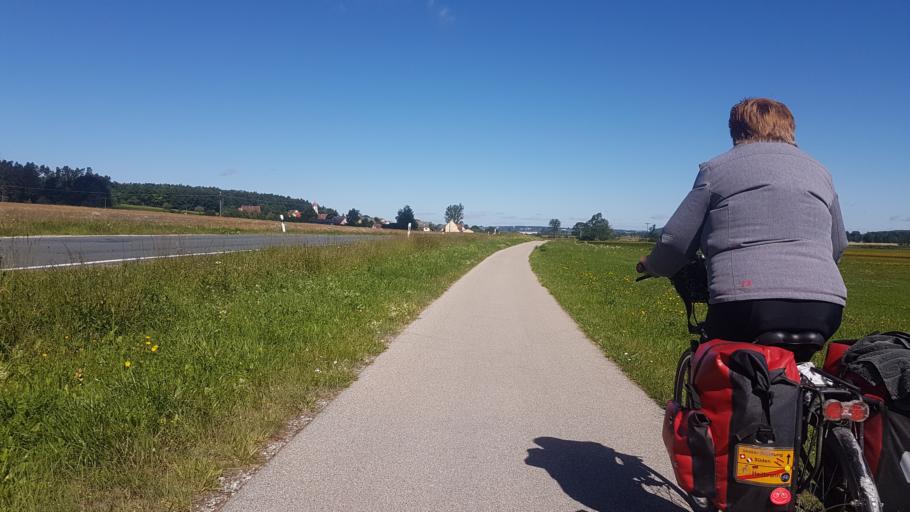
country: DE
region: Bavaria
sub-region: Regierungsbezirk Mittelfranken
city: Burgoberbach
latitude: 49.2014
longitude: 10.5573
